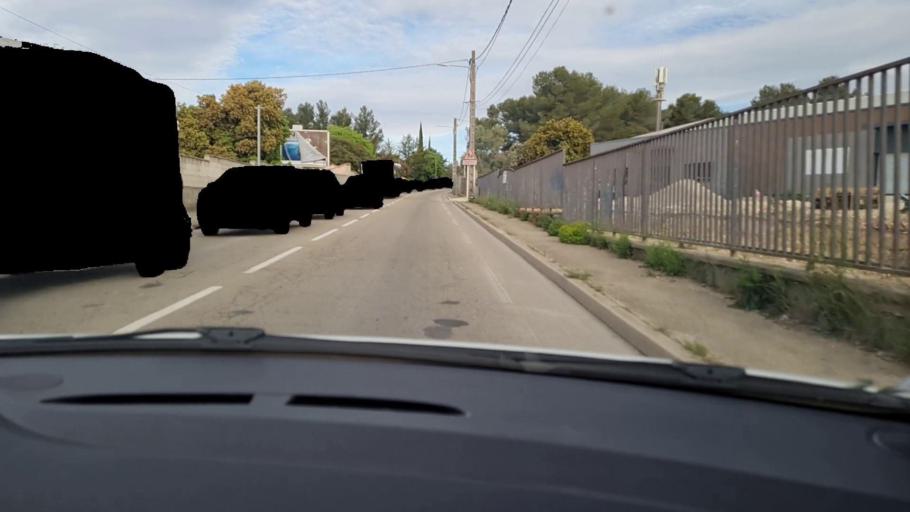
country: FR
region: Languedoc-Roussillon
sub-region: Departement du Gard
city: Nimes
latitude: 43.8426
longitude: 4.3121
